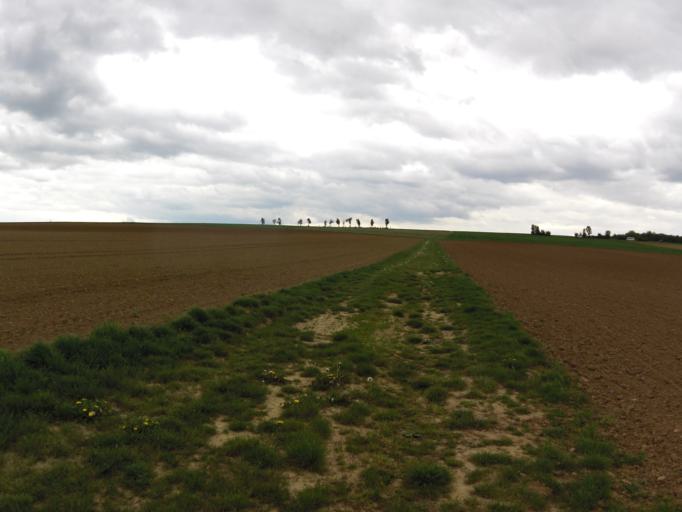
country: DE
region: Bavaria
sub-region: Regierungsbezirk Unterfranken
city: Oberpleichfeld
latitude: 49.8553
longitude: 10.0738
